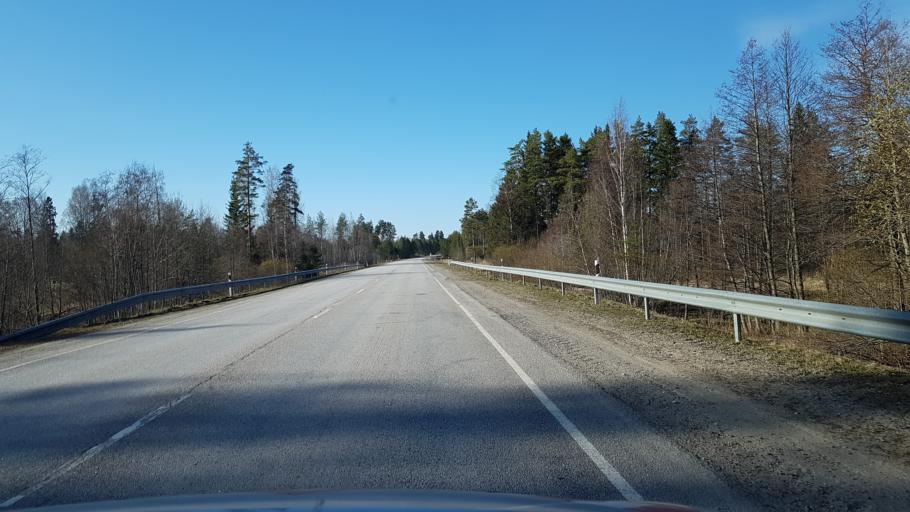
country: EE
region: Ida-Virumaa
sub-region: Johvi vald
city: Johvi
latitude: 59.1584
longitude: 27.3559
